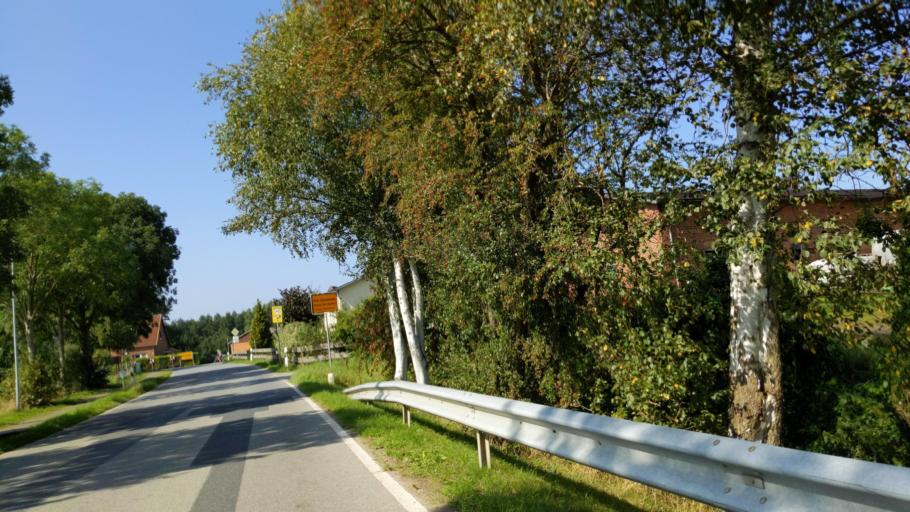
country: DE
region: Schleswig-Holstein
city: Gross Schenkenberg
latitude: 53.7964
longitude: 10.5627
